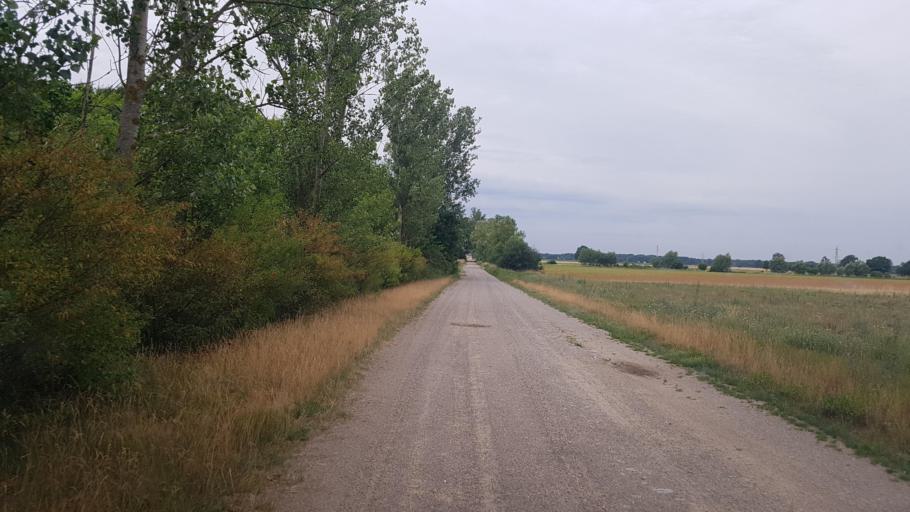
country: DE
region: Saxony-Anhalt
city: Holzdorf
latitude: 51.7577
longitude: 13.1857
